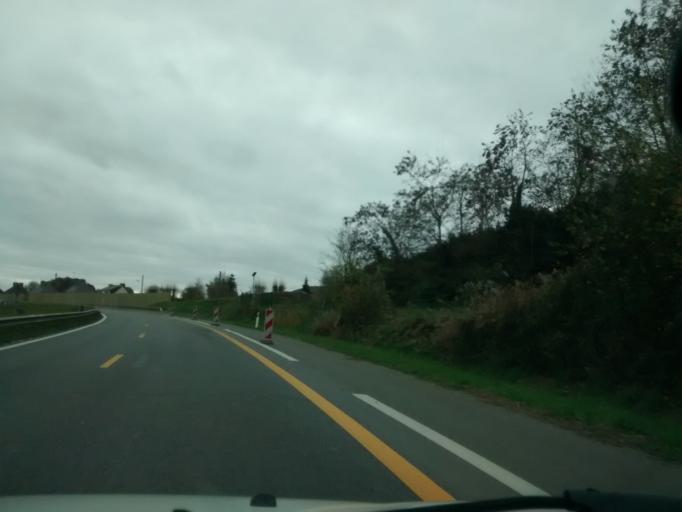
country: FR
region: Brittany
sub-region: Departement d'Ille-et-Vilaine
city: Saint-Pere
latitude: 48.5579
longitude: -1.9292
